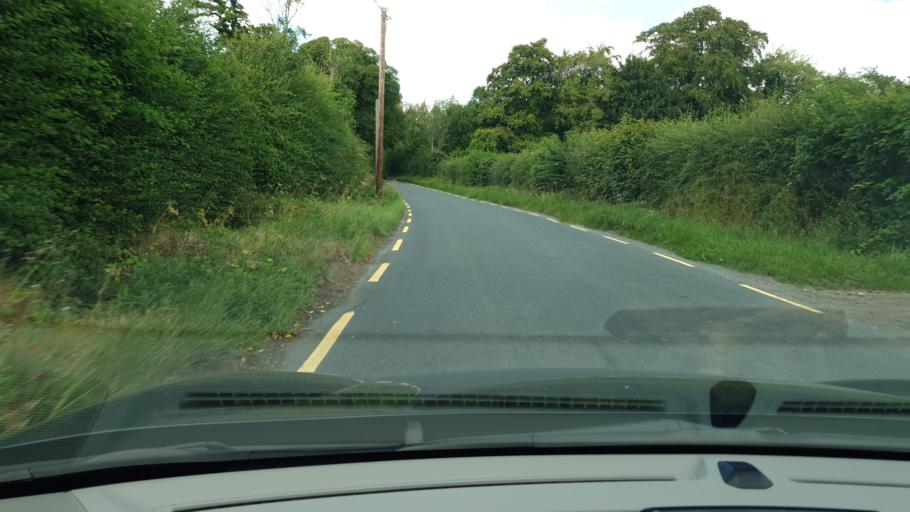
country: IE
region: Leinster
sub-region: An Mhi
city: Dunshaughlin
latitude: 53.5434
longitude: -6.6226
